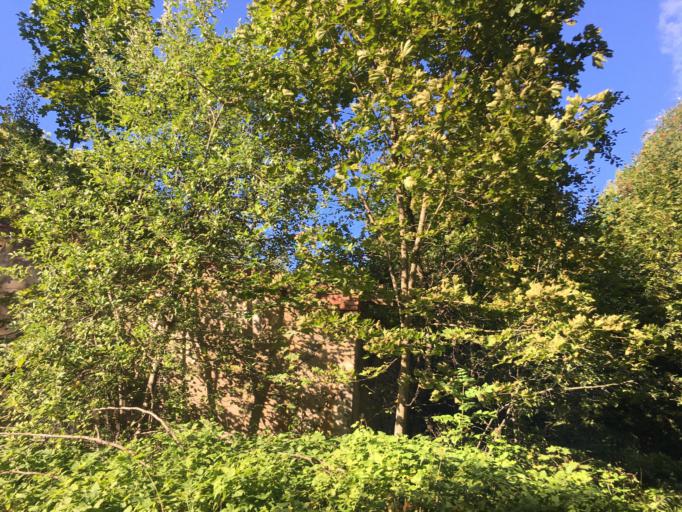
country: RU
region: Pskov
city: Izborsk
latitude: 57.7684
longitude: 27.9745
